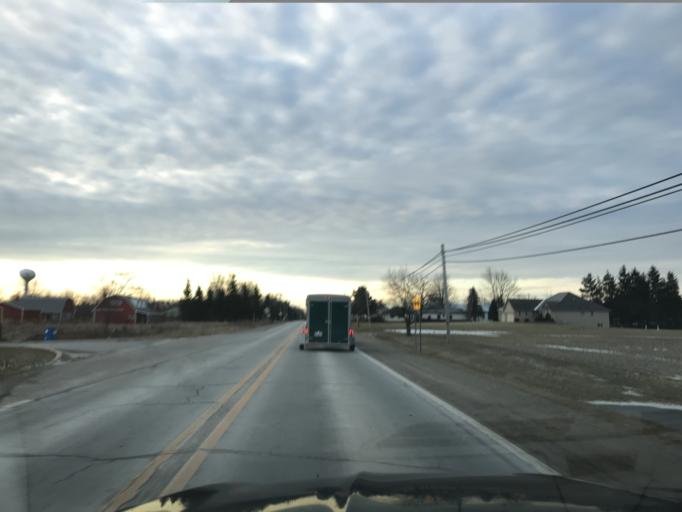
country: US
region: Michigan
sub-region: Macomb County
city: Armada
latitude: 42.8553
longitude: -82.8850
